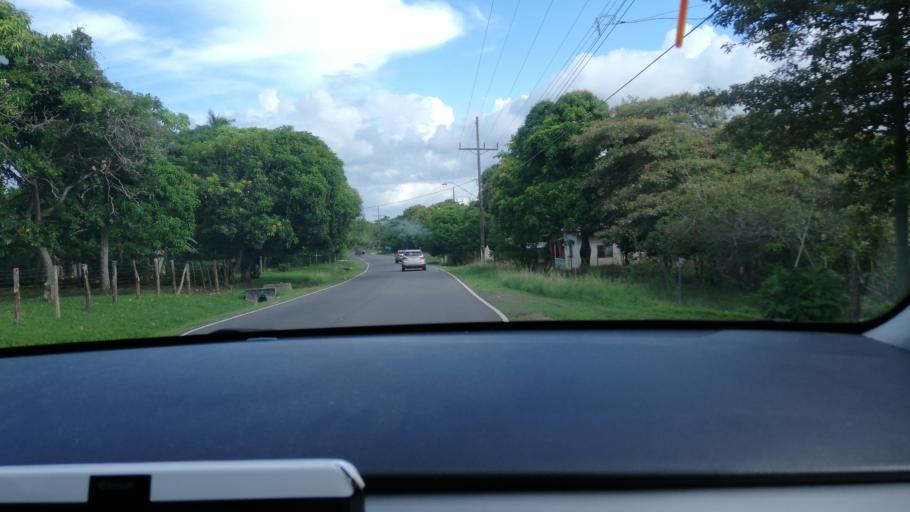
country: PA
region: Panama
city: Las Colinas
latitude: 8.5202
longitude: -80.0369
